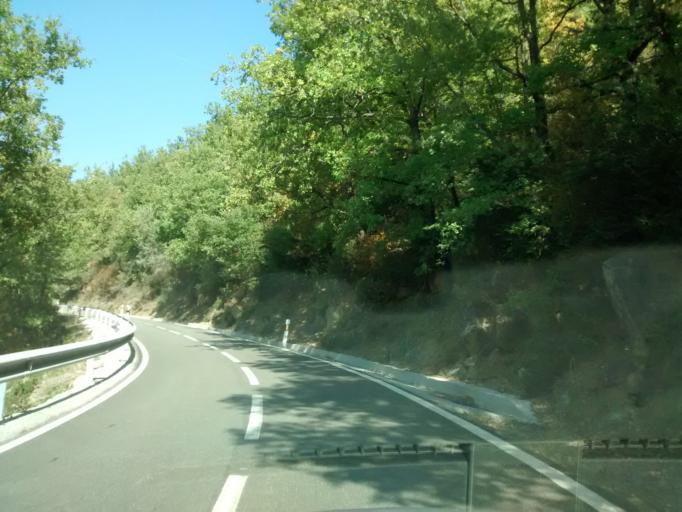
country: ES
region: Aragon
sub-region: Provincia de Huesca
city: Fiscal
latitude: 42.5286
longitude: -0.1331
